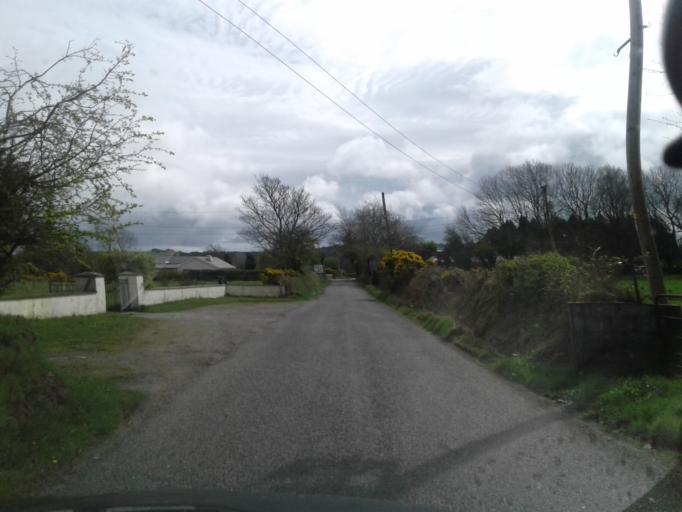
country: IE
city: Newtownmountkennedy
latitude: 53.0903
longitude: -6.2109
